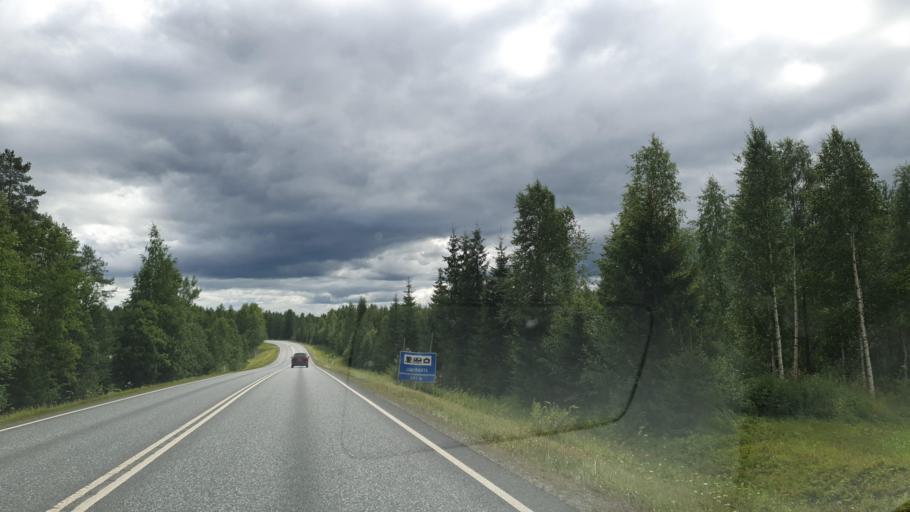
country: FI
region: Northern Savo
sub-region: Ylae-Savo
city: Sonkajaervi
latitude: 63.8080
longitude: 27.4183
